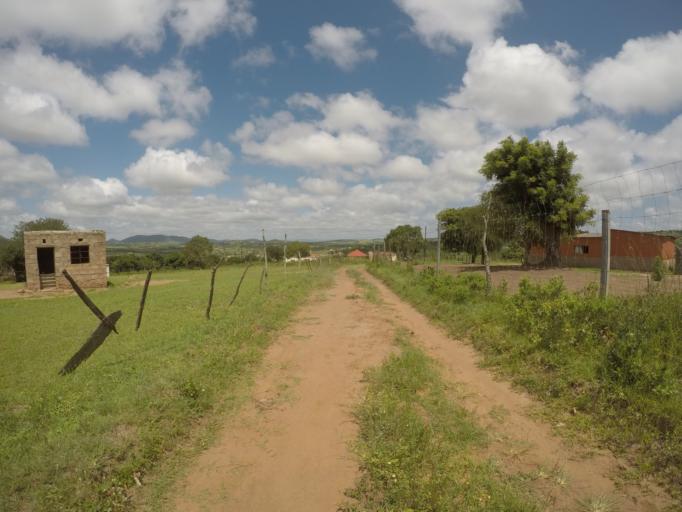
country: ZA
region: KwaZulu-Natal
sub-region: uThungulu District Municipality
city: Empangeni
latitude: -28.5788
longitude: 31.8417
